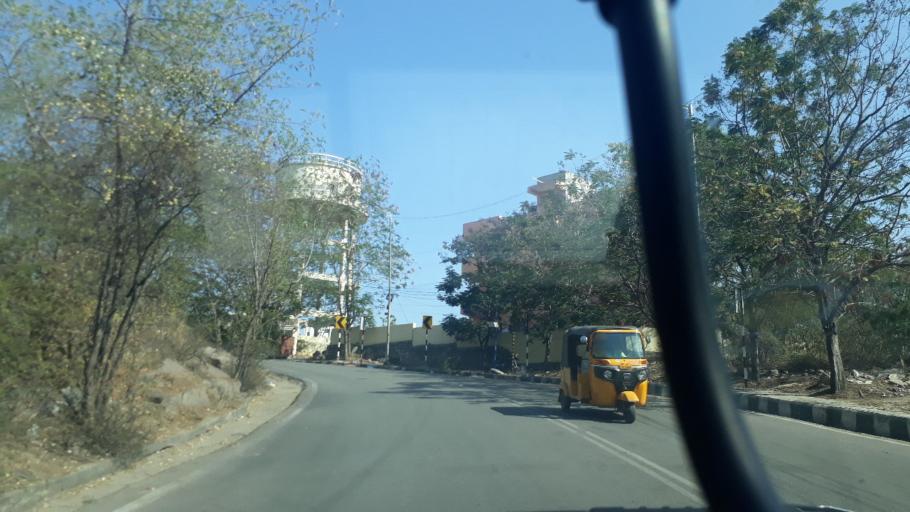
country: IN
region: Telangana
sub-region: Hyderabad
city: Hyderabad
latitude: 17.4176
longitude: 78.3974
